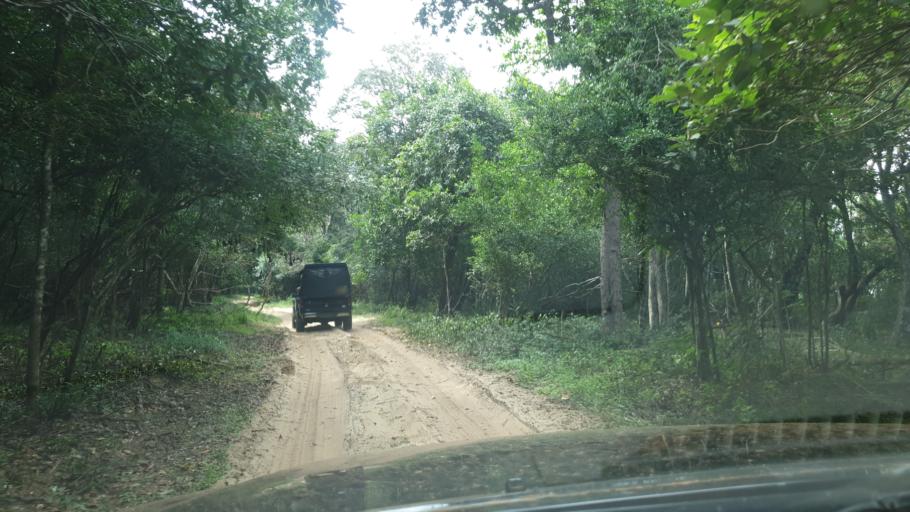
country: LK
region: North Western
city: Puttalam
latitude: 8.4125
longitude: 79.9900
